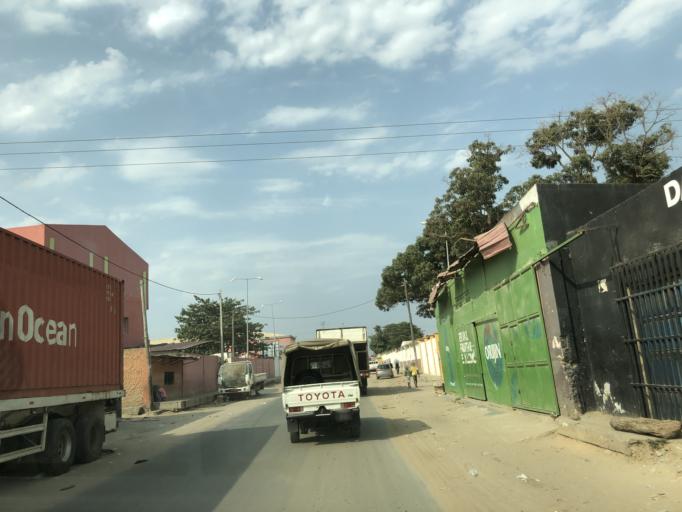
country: AO
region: Luanda
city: Luanda
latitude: -8.8936
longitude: 13.3533
